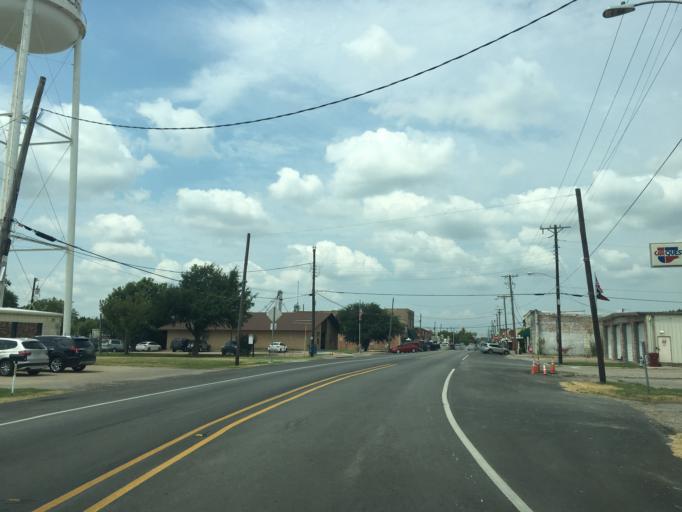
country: US
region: Texas
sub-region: Rockwall County
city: Royse City
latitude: 32.9759
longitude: -96.3296
